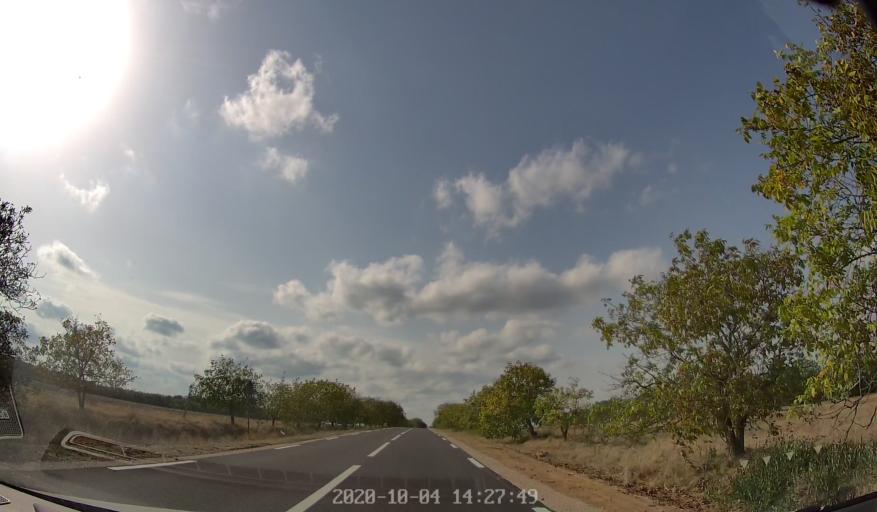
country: MD
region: Rezina
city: Saharna
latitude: 47.6321
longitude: 28.8586
